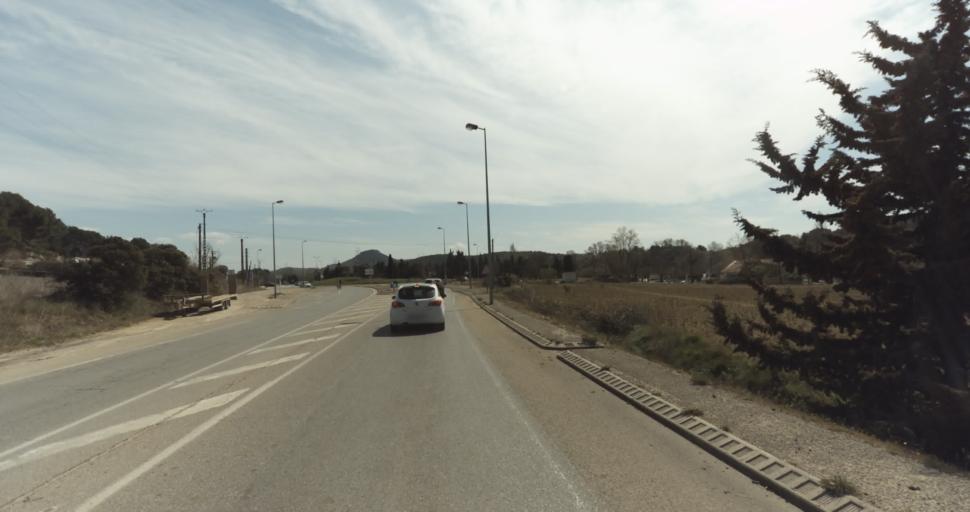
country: FR
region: Provence-Alpes-Cote d'Azur
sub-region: Departement des Bouches-du-Rhone
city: Velaux
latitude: 43.5434
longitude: 5.2586
